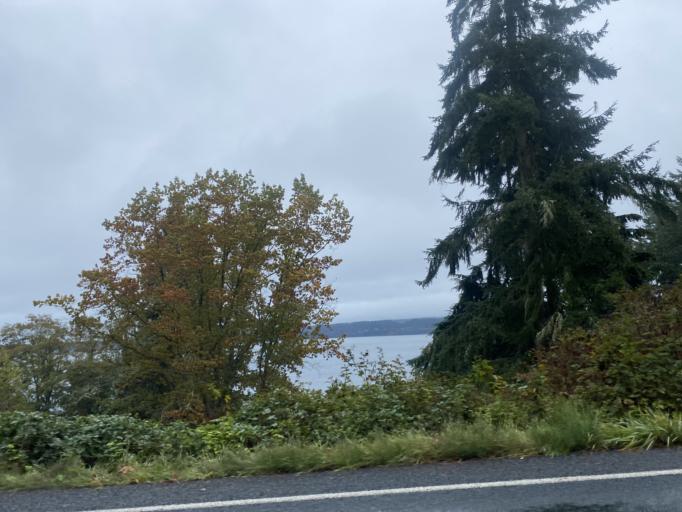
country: US
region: Washington
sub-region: Island County
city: Langley
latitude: 48.0447
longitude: -122.4333
